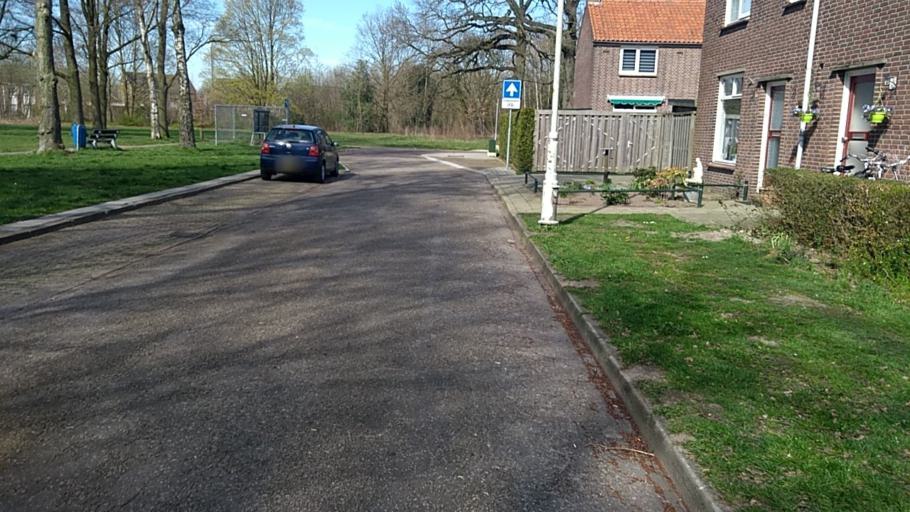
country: NL
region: Overijssel
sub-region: Gemeente Almelo
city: Almelo
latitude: 52.3701
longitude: 6.6895
